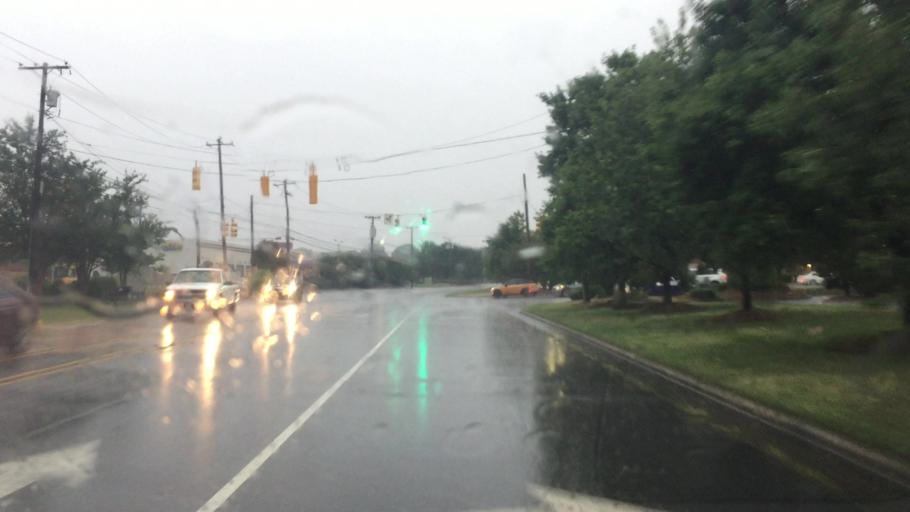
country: US
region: North Carolina
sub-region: Rowan County
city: Salisbury
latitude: 35.6527
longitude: -80.4582
